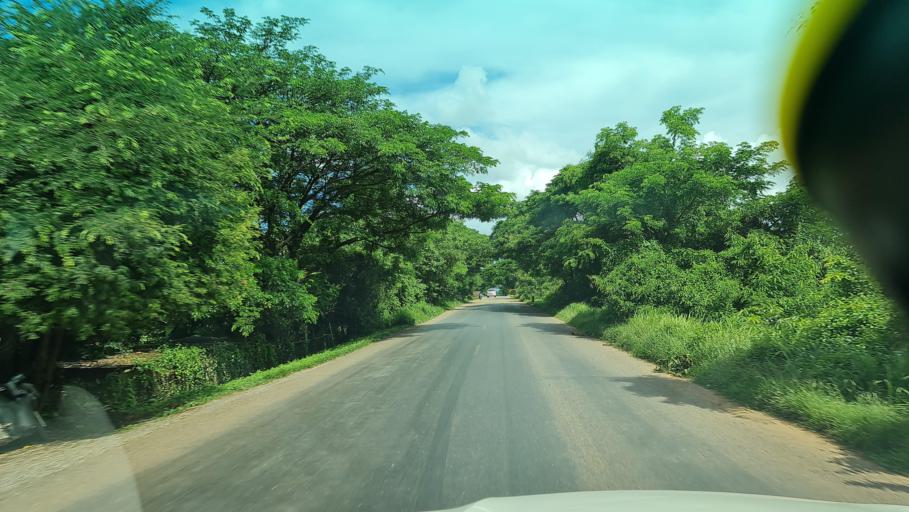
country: LA
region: Bolikhamxai
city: Ban Nahin
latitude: 18.2254
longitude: 104.1969
